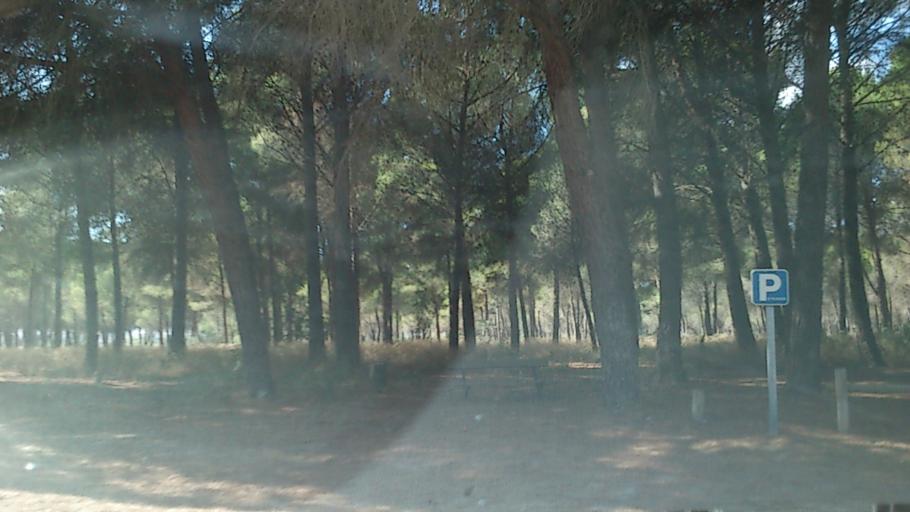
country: ES
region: Aragon
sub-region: Provincia de Zaragoza
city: Puebla de Alfinden
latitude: 41.6016
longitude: -0.7561
